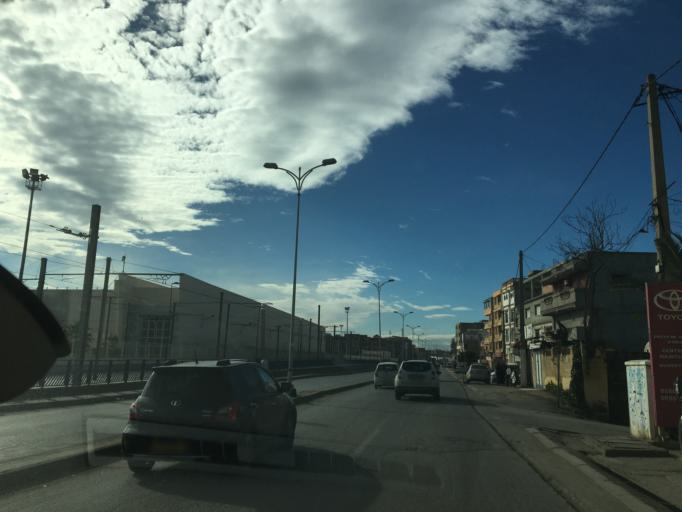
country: DZ
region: Alger
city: Bordj el Kiffan
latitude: 36.7504
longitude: 3.2115
